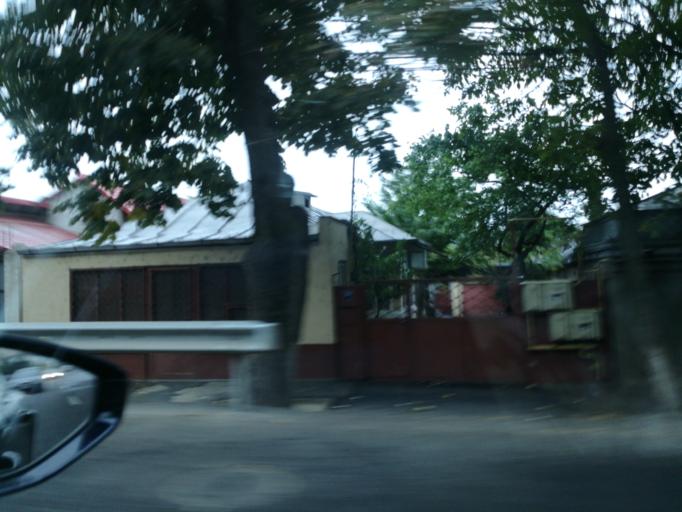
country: RO
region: Galati
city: Galati
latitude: 45.4686
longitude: 28.0342
